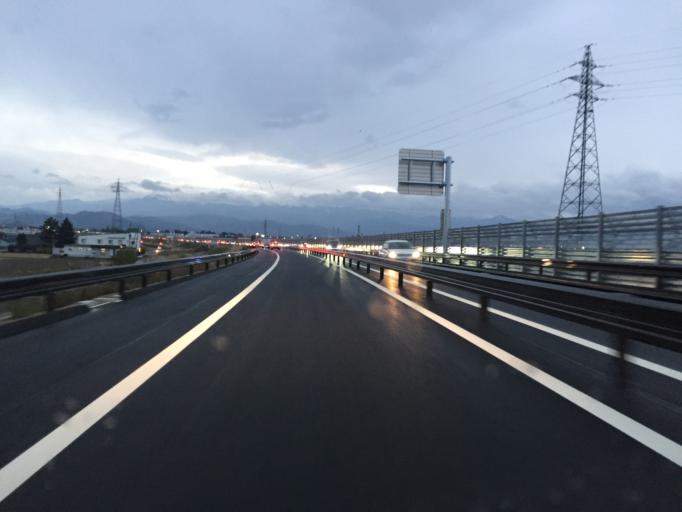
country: JP
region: Yamagata
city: Yonezawa
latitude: 37.9497
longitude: 140.1154
